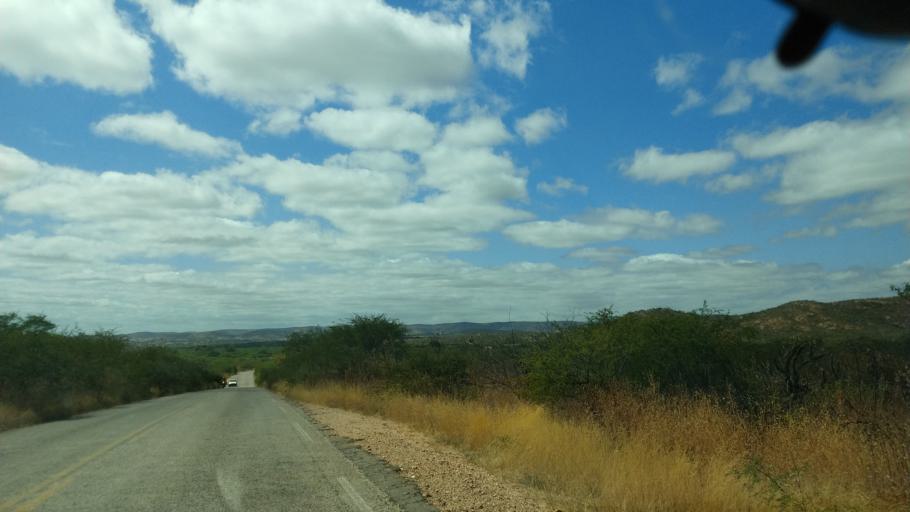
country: BR
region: Rio Grande do Norte
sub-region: Currais Novos
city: Currais Novos
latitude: -6.2609
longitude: -36.5728
